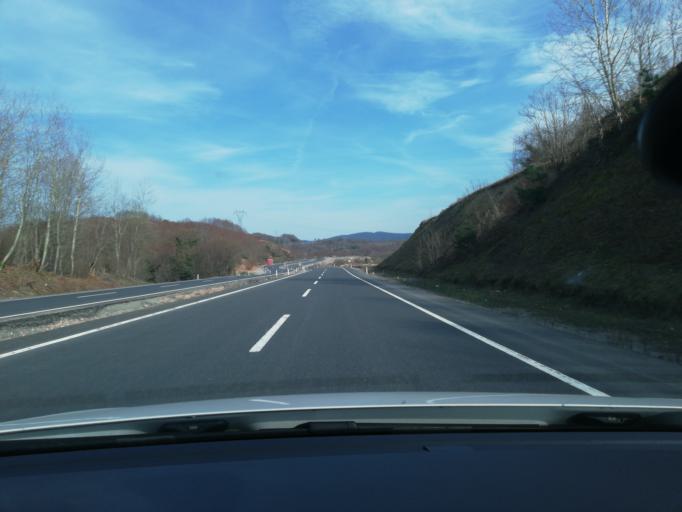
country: TR
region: Zonguldak
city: Eregli
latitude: 41.3313
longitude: 31.5768
